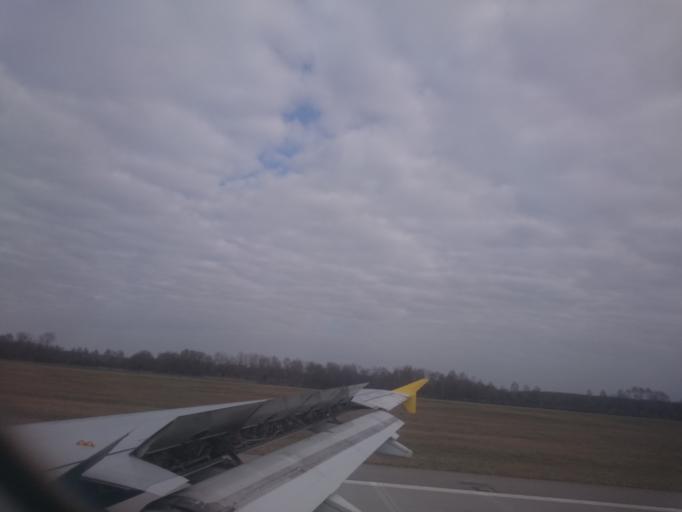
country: DE
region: Bavaria
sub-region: Upper Bavaria
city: Marzling
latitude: 48.3660
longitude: 11.8082
